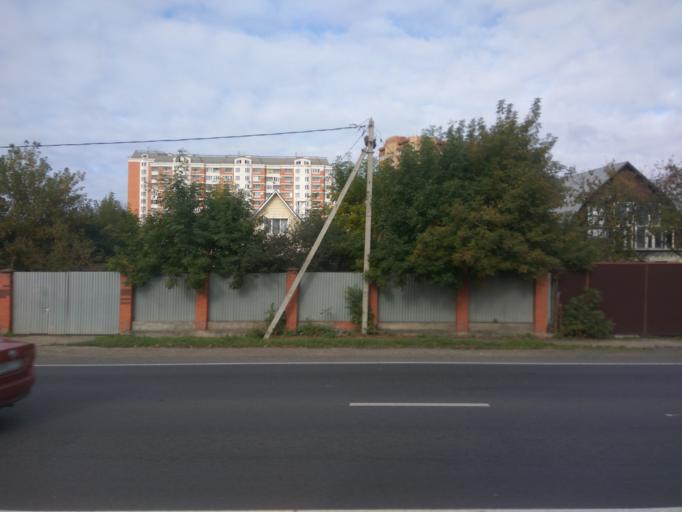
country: RU
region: Moskovskaya
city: Medvezh'i Ozera
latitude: 55.8644
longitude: 37.9901
